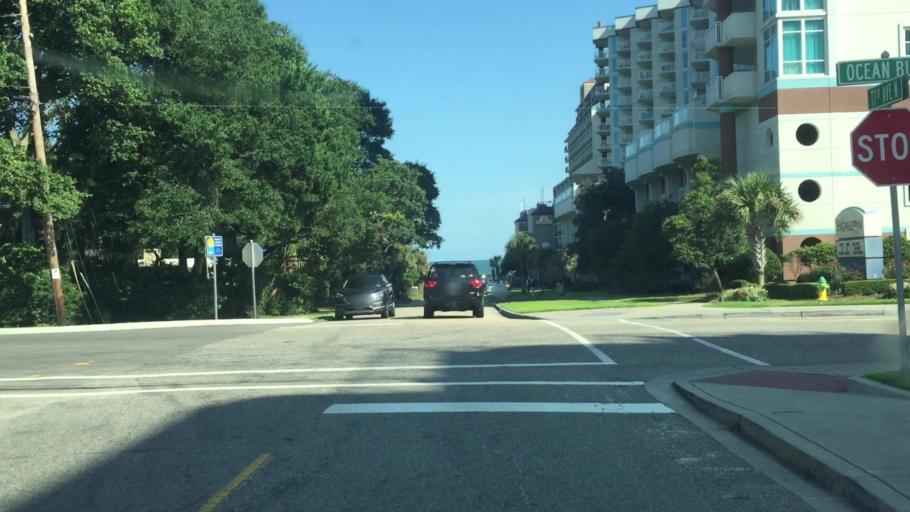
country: US
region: South Carolina
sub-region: Horry County
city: Myrtle Beach
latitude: 33.7454
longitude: -78.8154
